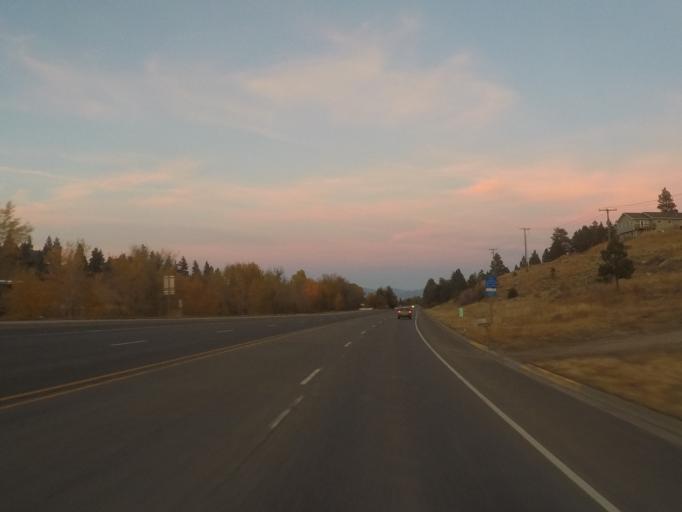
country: US
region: Montana
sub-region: Lewis and Clark County
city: Helena West Side
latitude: 46.5938
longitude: -112.1128
